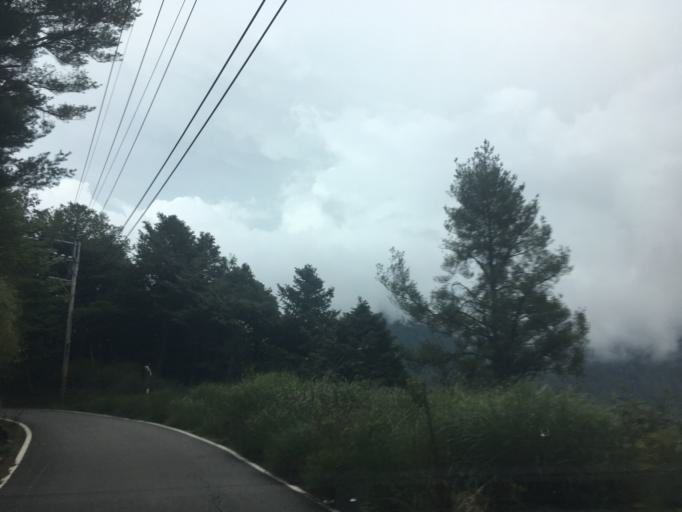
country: TW
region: Taiwan
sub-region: Nantou
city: Puli
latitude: 24.2743
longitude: 121.0324
